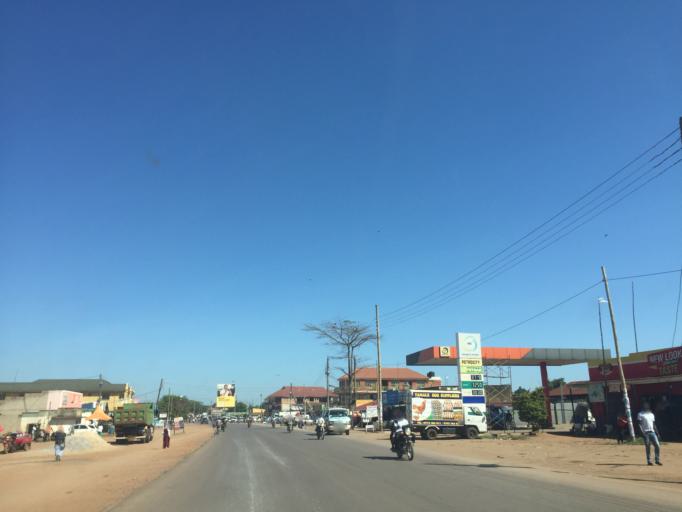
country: UG
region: Central Region
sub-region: Luwero District
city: Luwero
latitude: 0.8302
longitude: 32.5011
